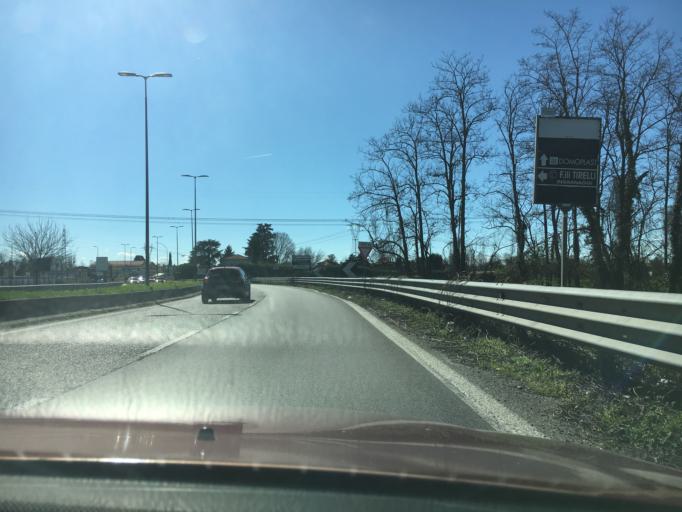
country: IT
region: Lombardy
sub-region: Citta metropolitana di Milano
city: Cusago
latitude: 45.4528
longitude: 9.0497
